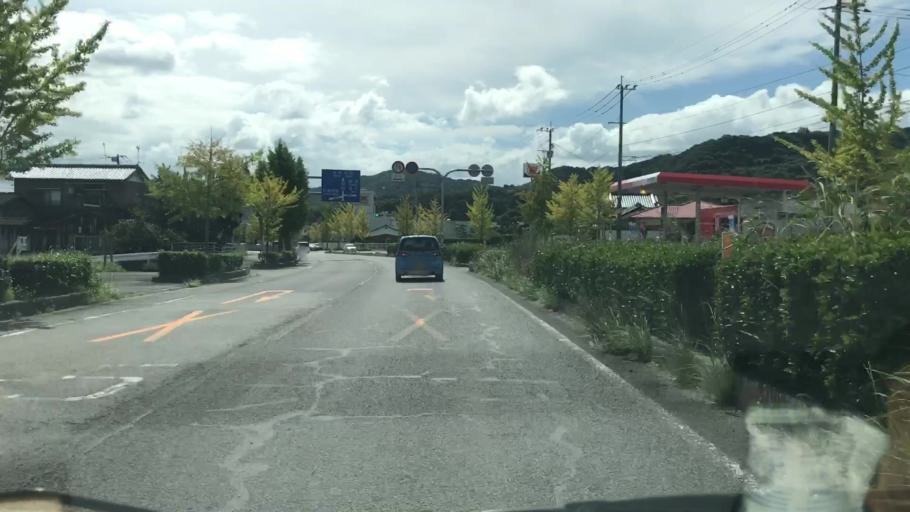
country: JP
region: Saga Prefecture
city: Saga-shi
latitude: 33.2440
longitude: 130.1871
